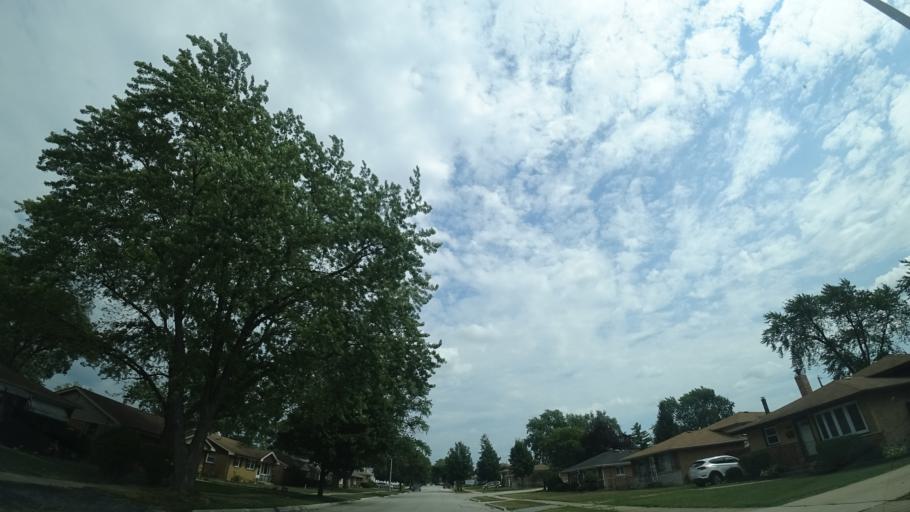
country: US
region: Illinois
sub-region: Cook County
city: Chicago Ridge
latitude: 41.6995
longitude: -87.7725
